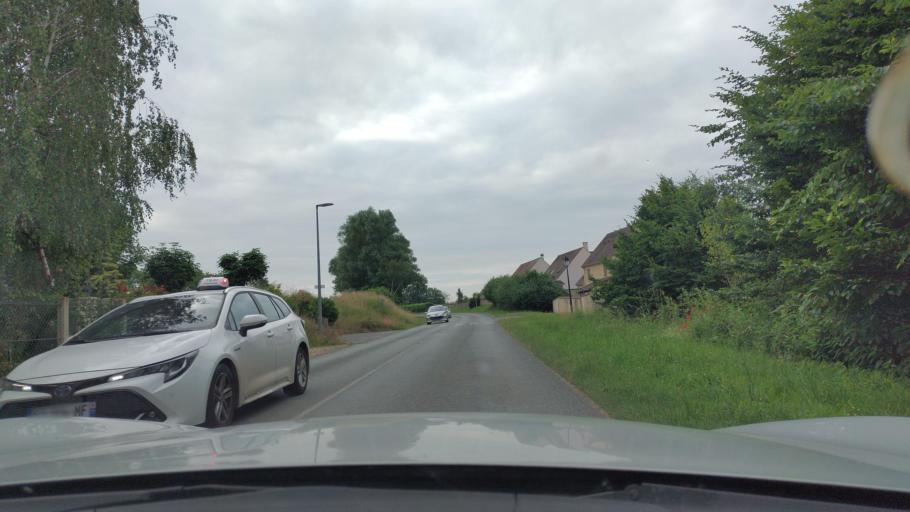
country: FR
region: Picardie
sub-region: Departement de l'Oise
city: Betz
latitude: 49.1016
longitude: 2.9595
